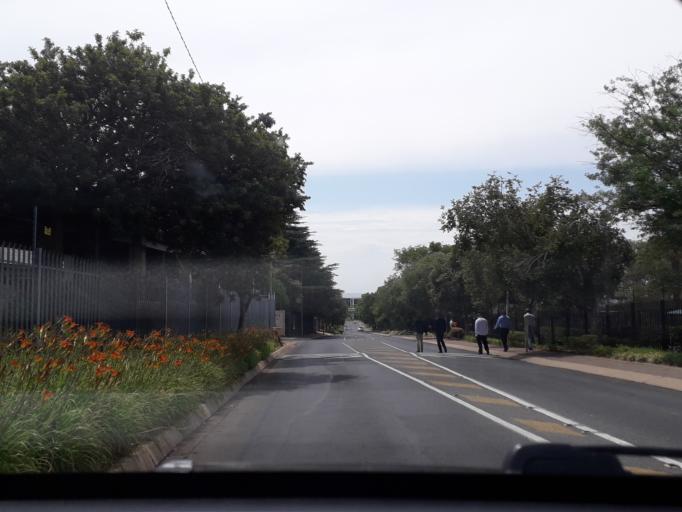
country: ZA
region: Gauteng
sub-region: City of Johannesburg Metropolitan Municipality
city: Diepsloot
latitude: -26.0445
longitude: 28.0209
